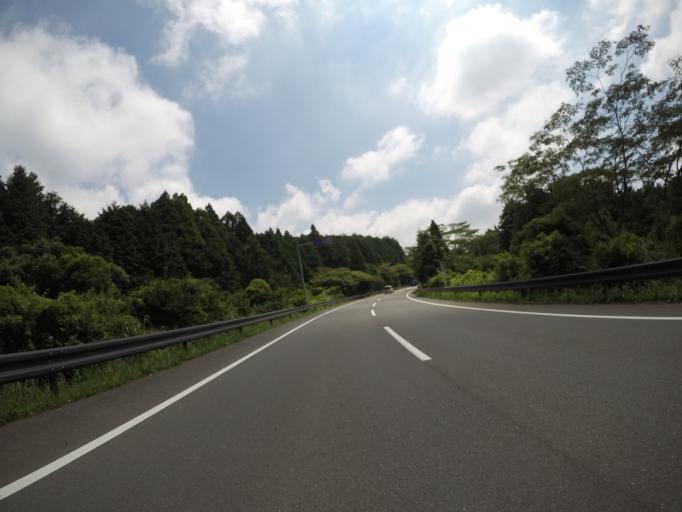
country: JP
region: Shizuoka
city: Fujinomiya
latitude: 35.2543
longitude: 138.6868
